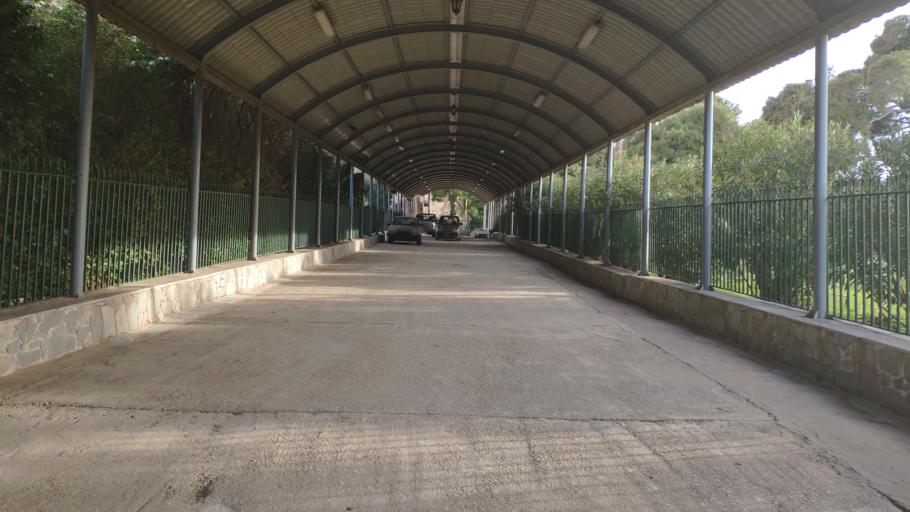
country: GR
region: Attica
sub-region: Nomarchia Dytikis Attikis
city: Nea Peramos
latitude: 37.9842
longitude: 23.4355
